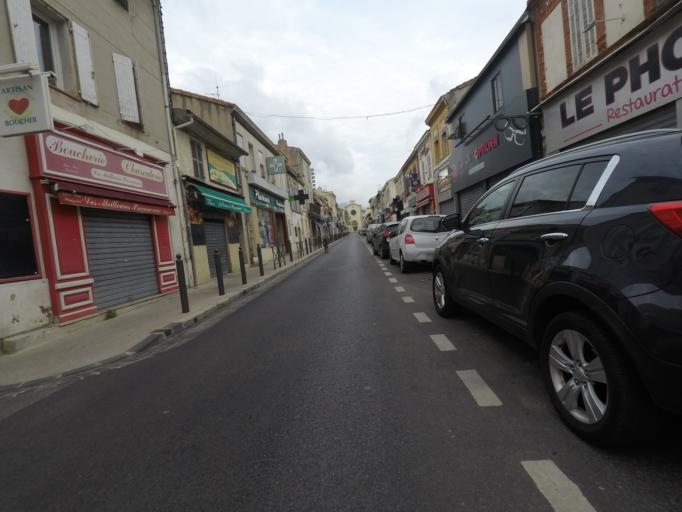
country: FR
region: Provence-Alpes-Cote d'Azur
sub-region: Departement des Bouches-du-Rhone
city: Marseille 09
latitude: 43.2470
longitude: 5.4018
